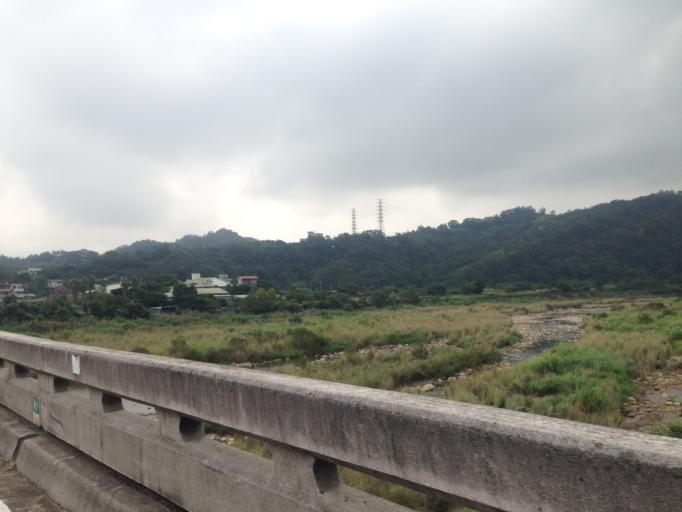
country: TW
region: Taiwan
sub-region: Hsinchu
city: Hsinchu
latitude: 24.6764
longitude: 120.9482
